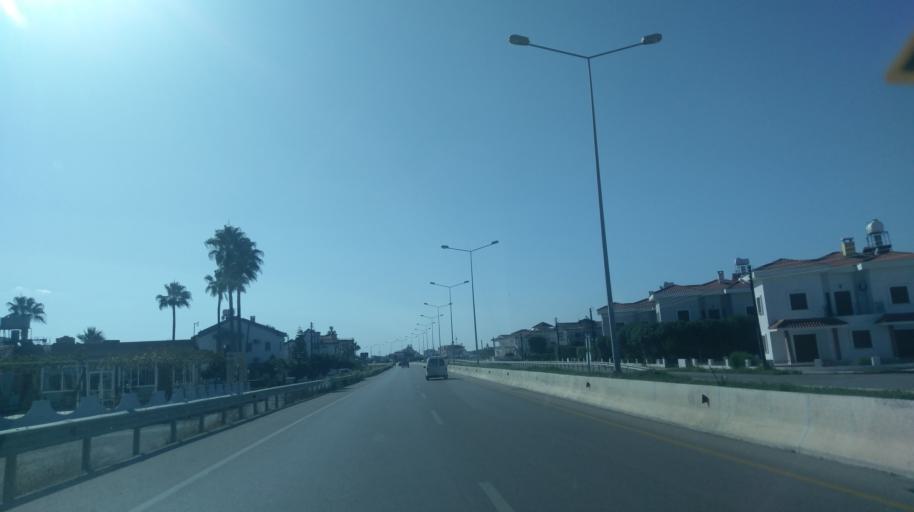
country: CY
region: Ammochostos
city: Trikomo
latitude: 35.2161
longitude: 33.8944
